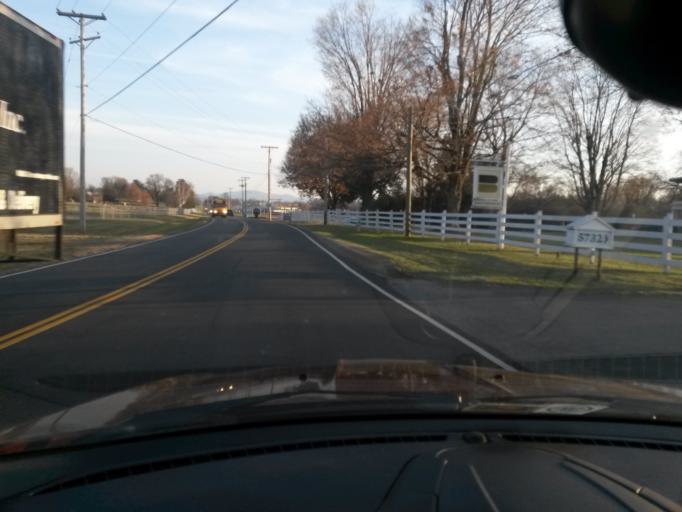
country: US
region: Virginia
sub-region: Roanoke County
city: Hollins
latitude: 37.3280
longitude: -79.9671
